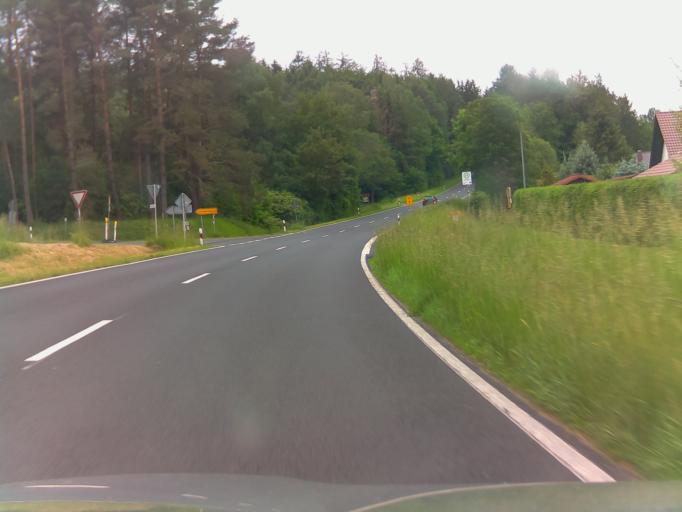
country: DE
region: Bavaria
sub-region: Regierungsbezirk Unterfranken
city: Oberleichtersbach
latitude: 50.2594
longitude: 9.8187
